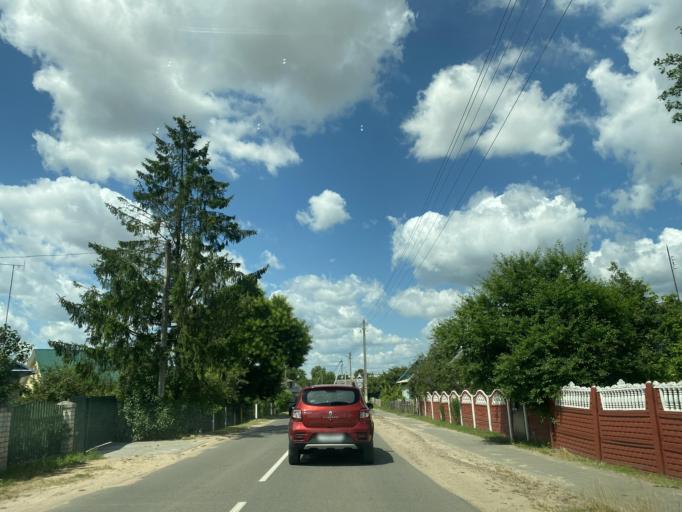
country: BY
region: Brest
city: Ivanava
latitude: 52.1438
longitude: 25.5435
